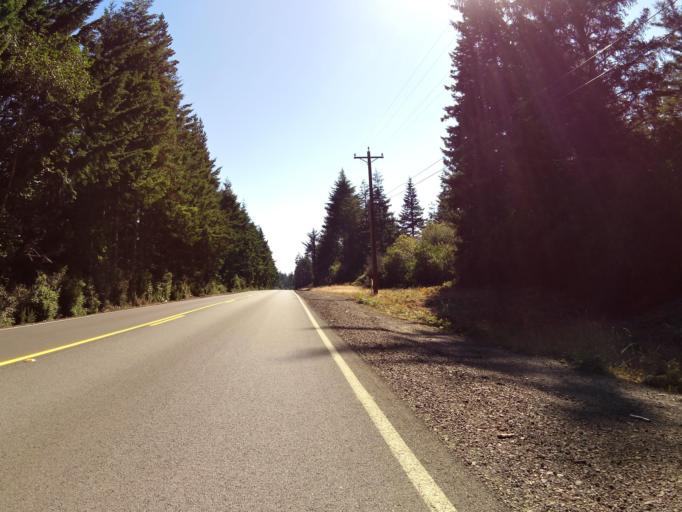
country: US
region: Oregon
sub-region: Coos County
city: Bandon
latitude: 43.2009
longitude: -124.3661
